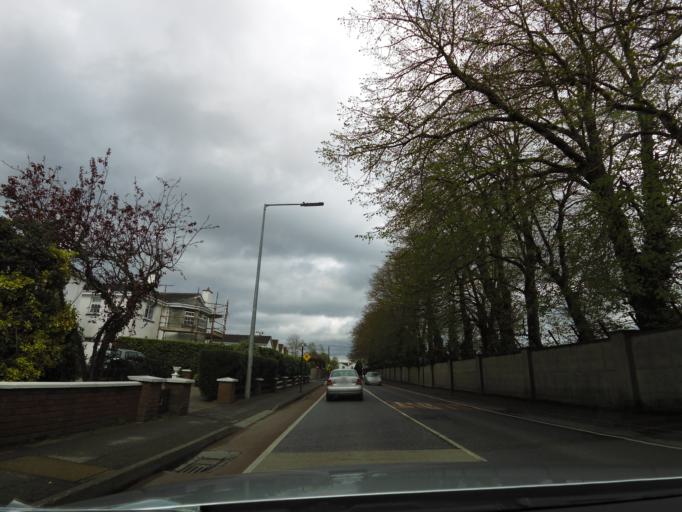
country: IE
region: Leinster
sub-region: Kilkenny
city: Kilkenny
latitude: 52.6632
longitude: -7.2649
